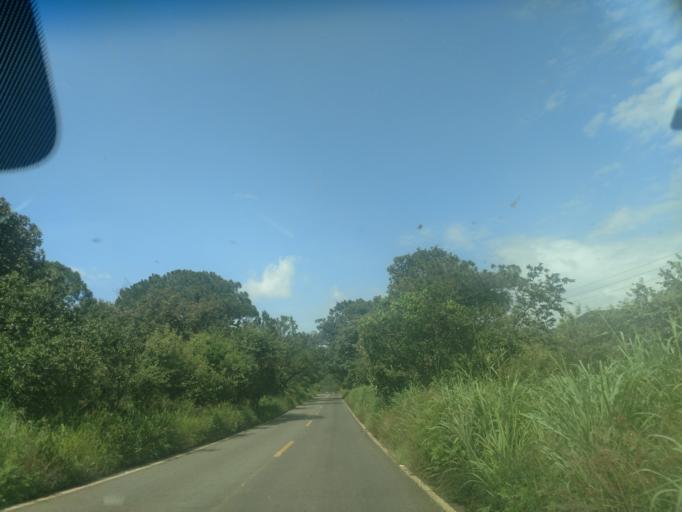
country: MX
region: Jalisco
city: Talpa de Allende
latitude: 20.4354
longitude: -104.7821
